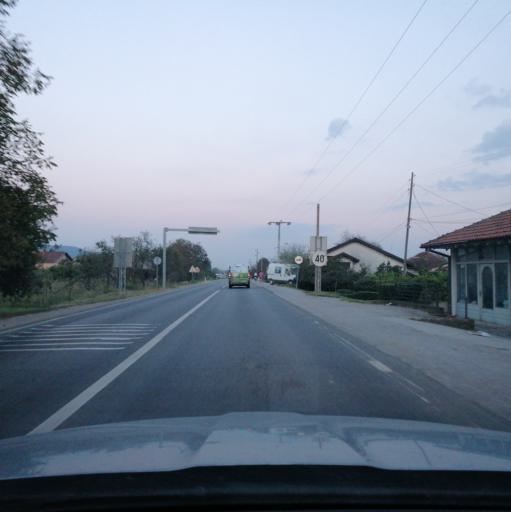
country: RS
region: Central Serbia
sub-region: Raski Okrug
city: Vrnjacka Banja
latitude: 43.6509
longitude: 20.8823
